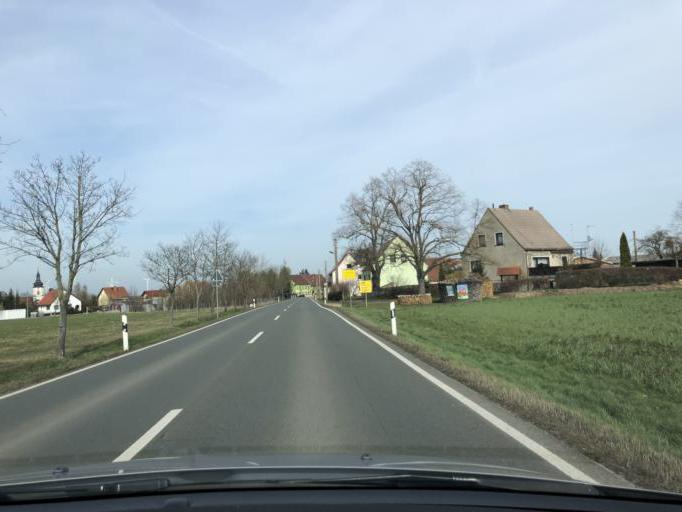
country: DE
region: Thuringia
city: Gosen
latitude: 50.9981
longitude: 11.9071
